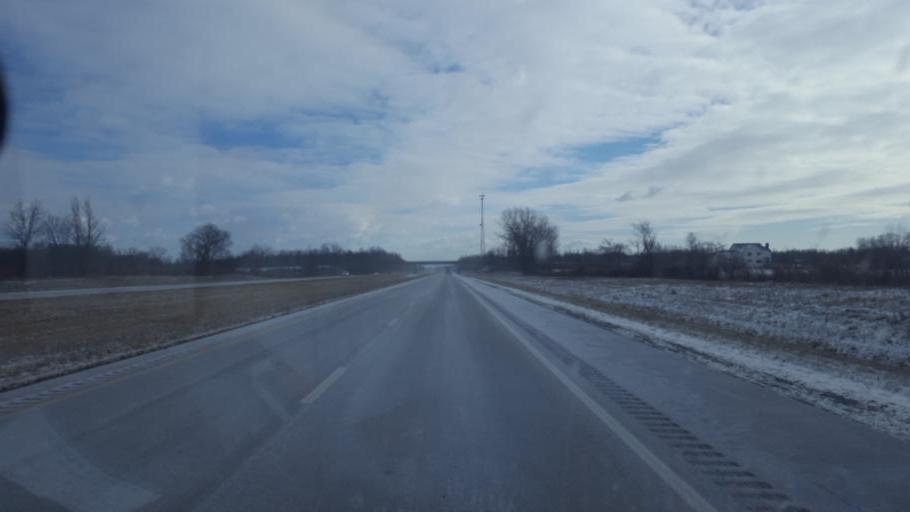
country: US
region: Ohio
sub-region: Licking County
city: Etna
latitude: 39.9463
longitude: -82.6333
